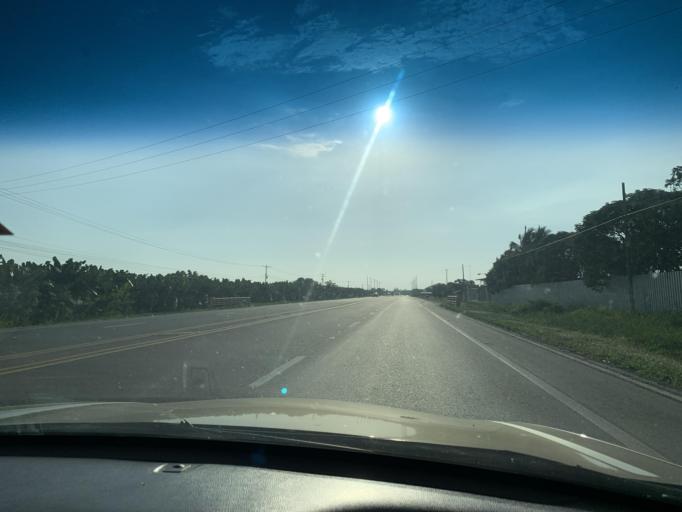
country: EC
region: Guayas
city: Naranjito
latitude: -2.2548
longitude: -79.6151
